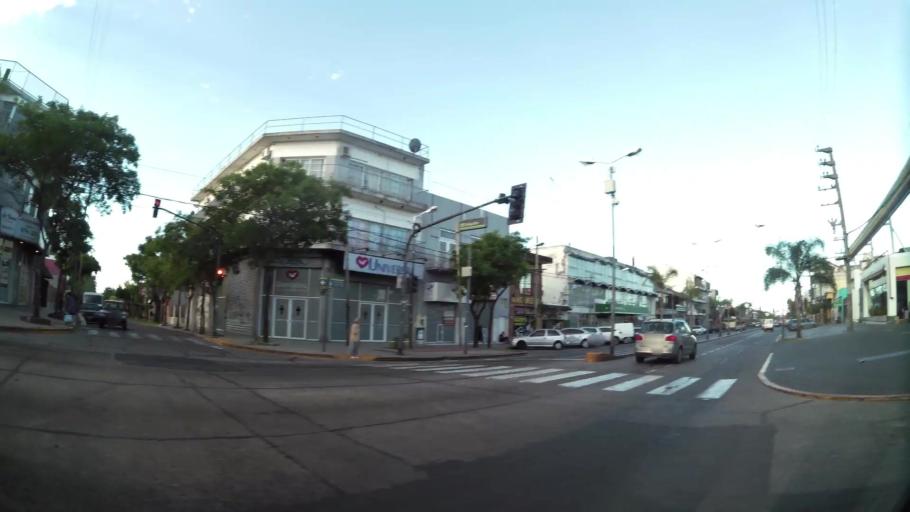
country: AR
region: Buenos Aires
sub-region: Partido de Tigre
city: Tigre
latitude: -34.4581
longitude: -58.5672
